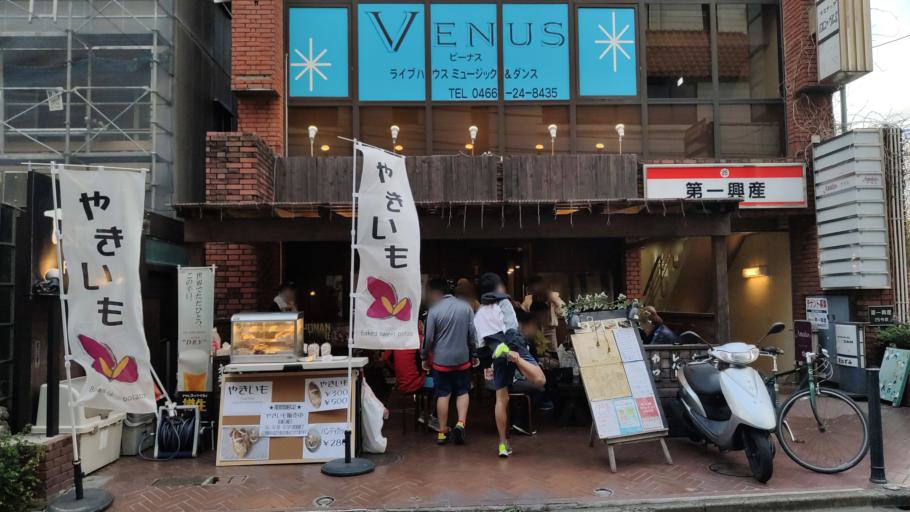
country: JP
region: Kanagawa
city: Fujisawa
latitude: 35.3376
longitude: 139.4856
